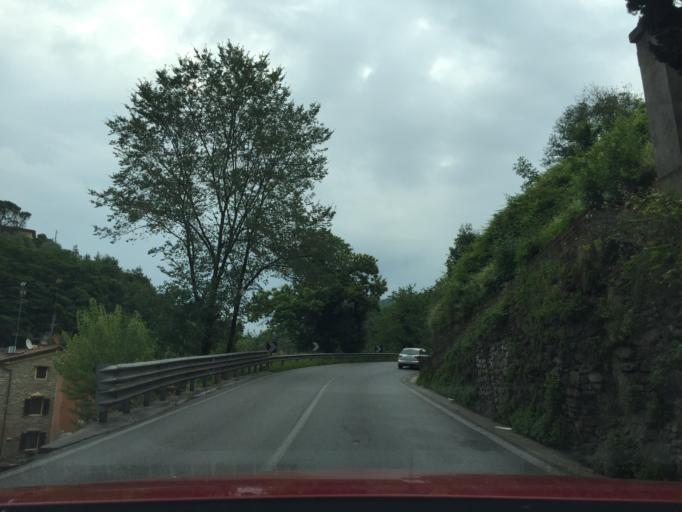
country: IT
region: Tuscany
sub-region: Provincia di Pistoia
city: Serravalle Pistoiese
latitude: 43.9020
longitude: 10.8267
